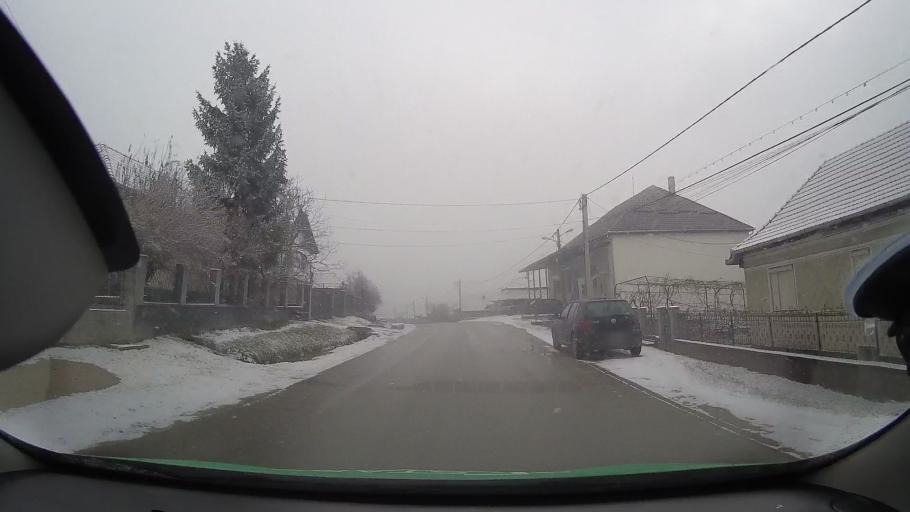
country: RO
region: Alba
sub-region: Comuna Lopadea Noua
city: Lopadea Noua
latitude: 46.2922
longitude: 23.8190
